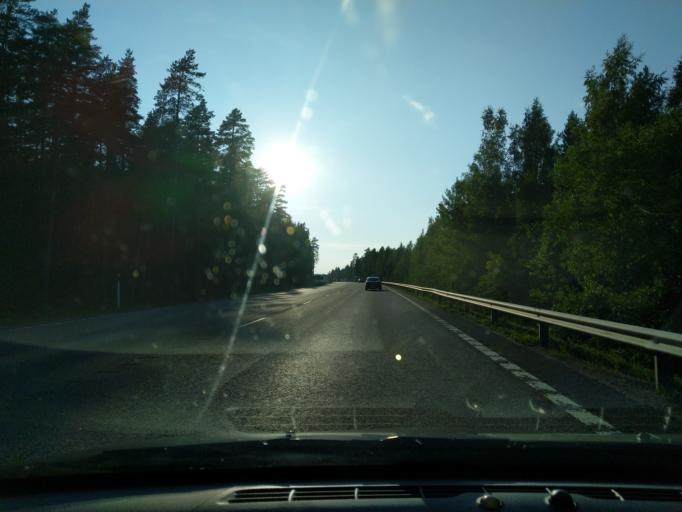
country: FI
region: Paijanne Tavastia
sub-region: Lahti
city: Lahti
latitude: 60.9654
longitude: 25.7433
